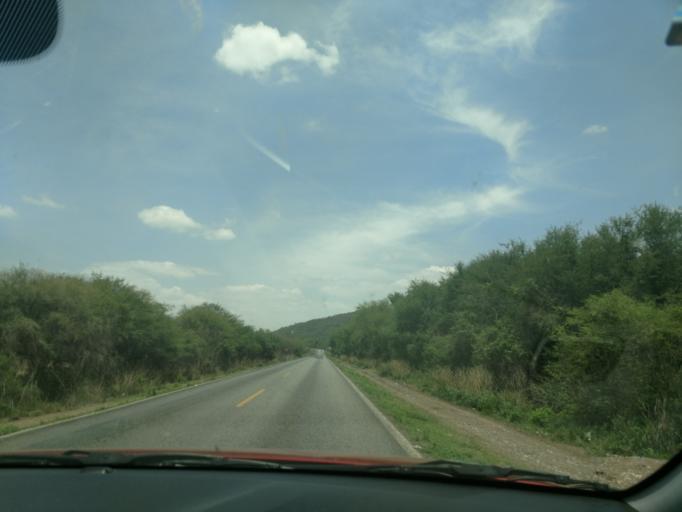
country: MX
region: San Luis Potosi
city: Ciudad Fernandez
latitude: 21.9978
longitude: -100.1399
